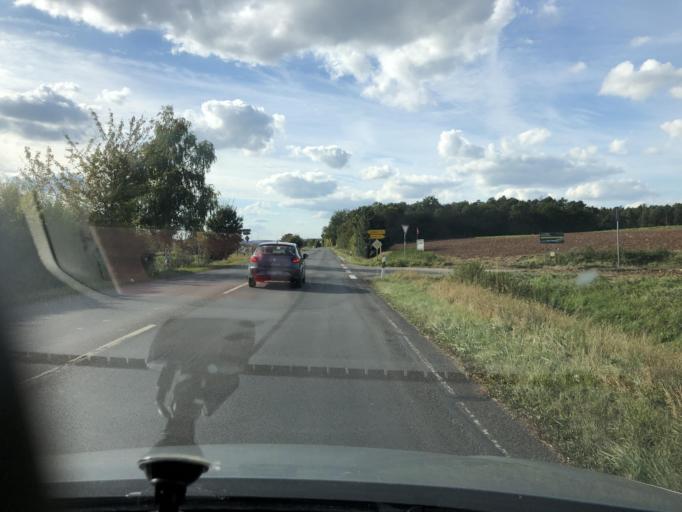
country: DE
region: Bavaria
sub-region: Regierungsbezirk Mittelfranken
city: Puschendorf
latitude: 49.4929
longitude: 10.8318
